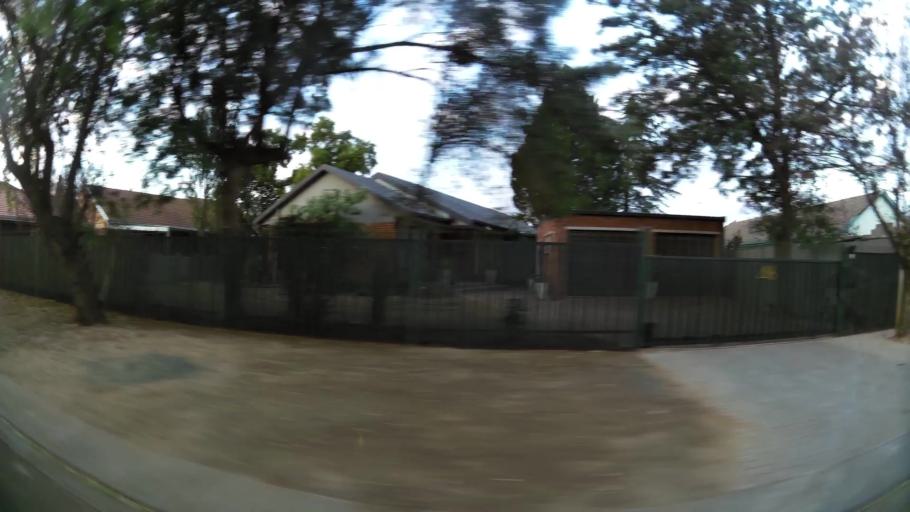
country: ZA
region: Orange Free State
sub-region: Mangaung Metropolitan Municipality
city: Bloemfontein
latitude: -29.1677
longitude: 26.1850
